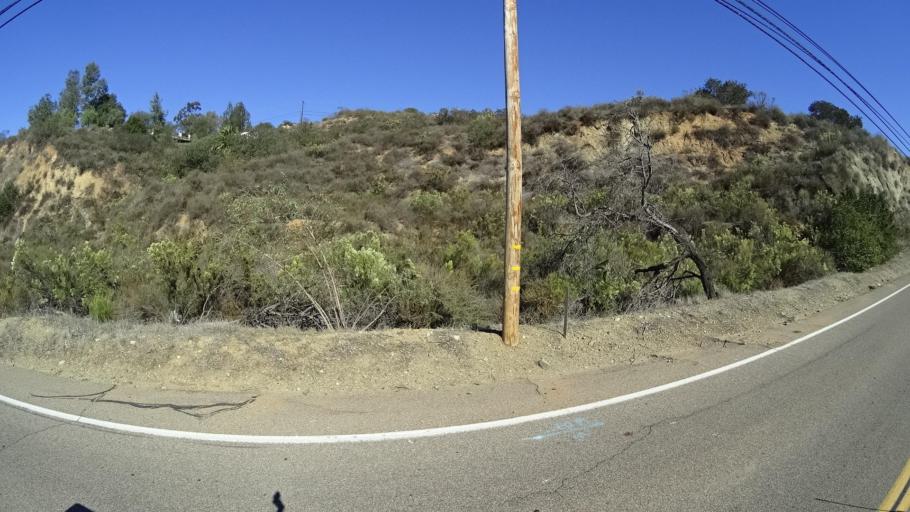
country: US
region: California
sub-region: San Diego County
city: Jamul
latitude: 32.7212
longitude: -116.8770
